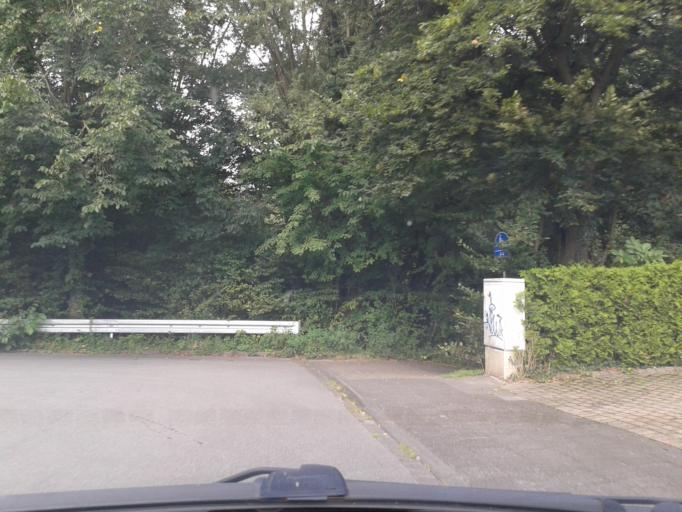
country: DE
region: North Rhine-Westphalia
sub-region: Regierungsbezirk Detmold
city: Paderborn
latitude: 51.7266
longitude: 8.7384
